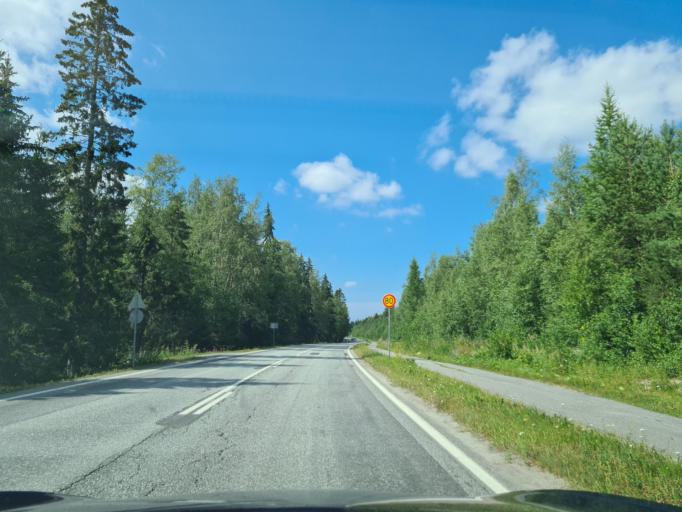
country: FI
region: Ostrobothnia
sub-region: Vaasa
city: Vaasa
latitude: 63.1958
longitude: 21.5465
